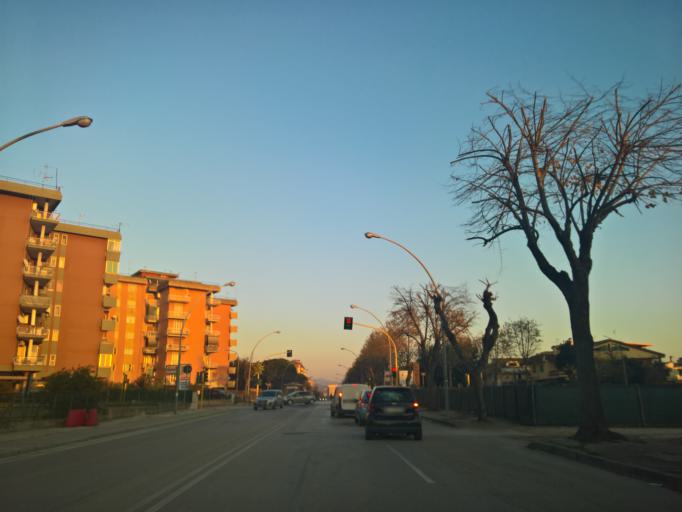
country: IT
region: Campania
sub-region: Provincia di Caserta
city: Santa Maria Capua Vetere
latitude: 41.0899
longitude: 14.2575
